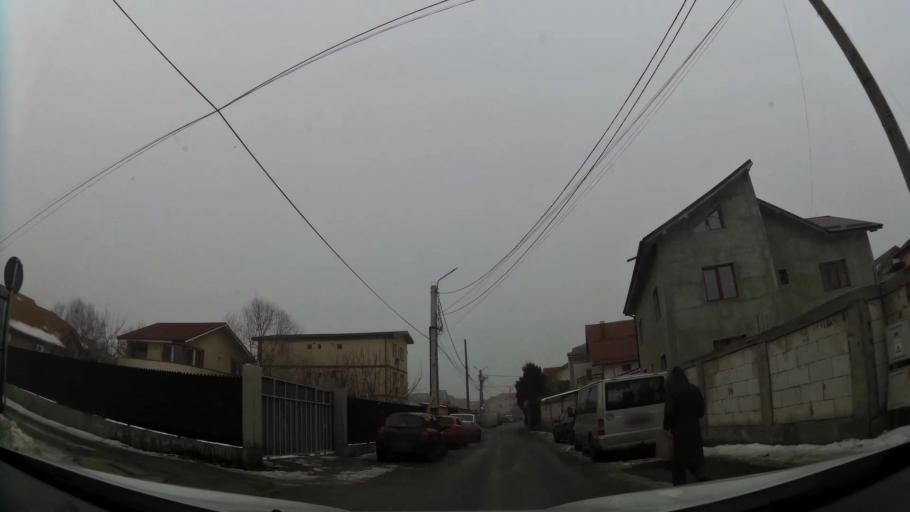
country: RO
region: Ilfov
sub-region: Comuna Chiajna
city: Rosu
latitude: 44.4453
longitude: 26.0079
